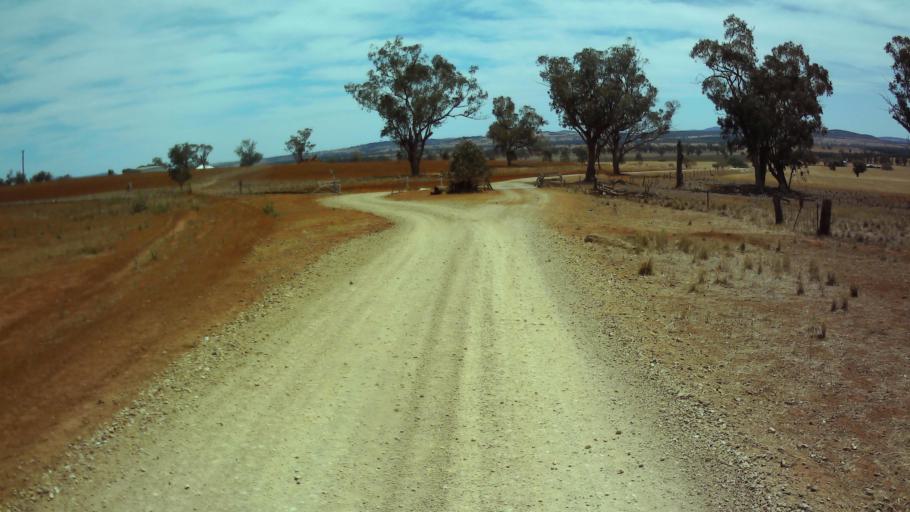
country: AU
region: New South Wales
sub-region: Weddin
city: Grenfell
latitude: -33.7501
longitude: 148.1560
